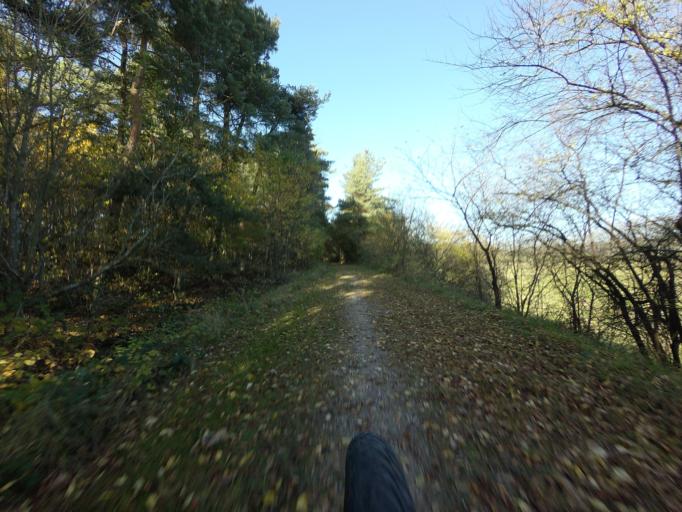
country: DK
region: Central Jutland
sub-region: Syddjurs Kommune
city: Ryomgard
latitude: 56.4807
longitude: 10.6420
